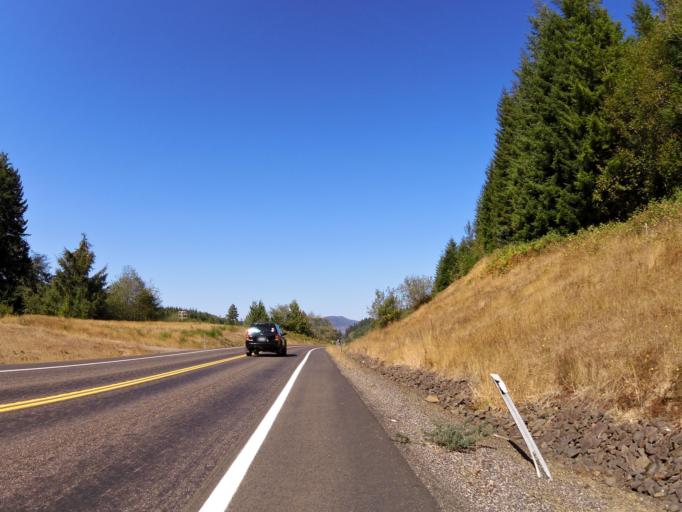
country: US
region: Oregon
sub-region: Tillamook County
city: Tillamook
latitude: 45.3223
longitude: -123.8443
